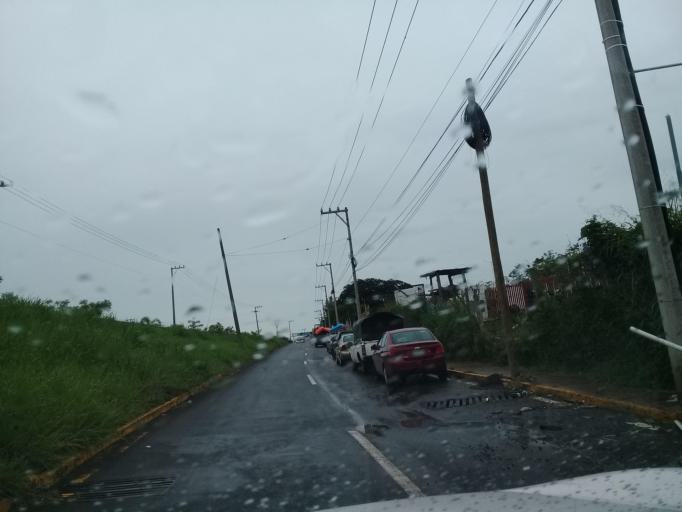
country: MX
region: Veracruz
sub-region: Emiliano Zapata
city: Las Trancas
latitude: 19.5073
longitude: -96.8548
